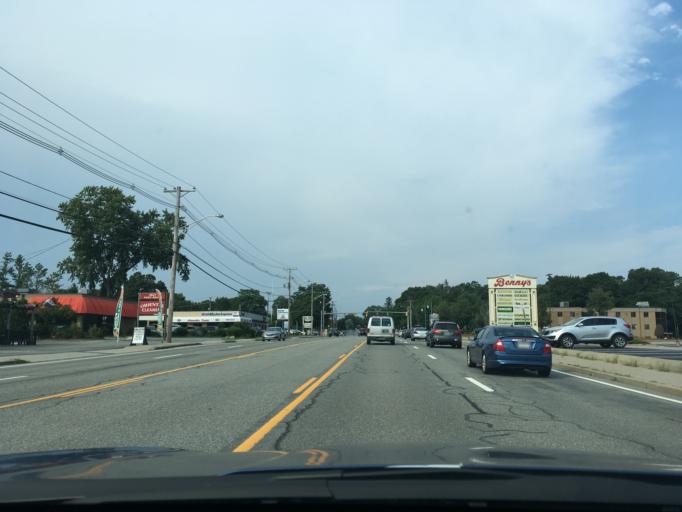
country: US
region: Rhode Island
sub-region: Kent County
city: East Greenwich
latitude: 41.6417
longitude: -71.4674
